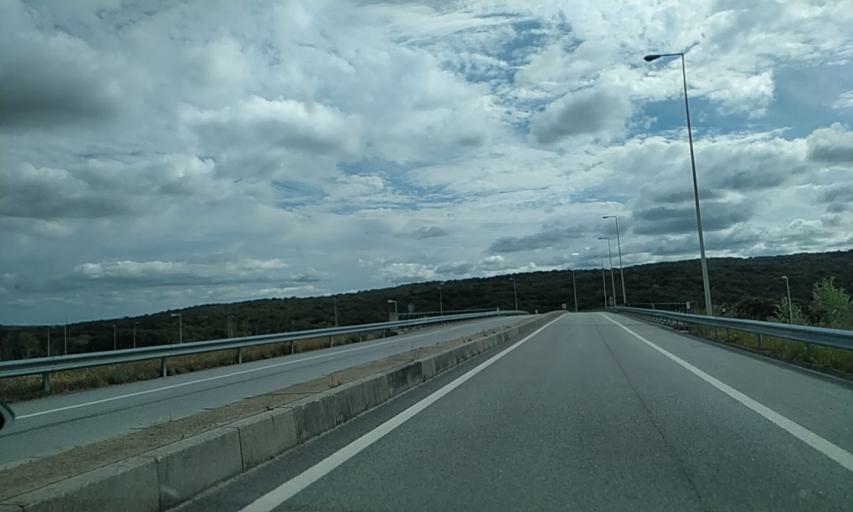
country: PT
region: Evora
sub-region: Evora
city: Evora
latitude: 38.5956
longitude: -8.0233
